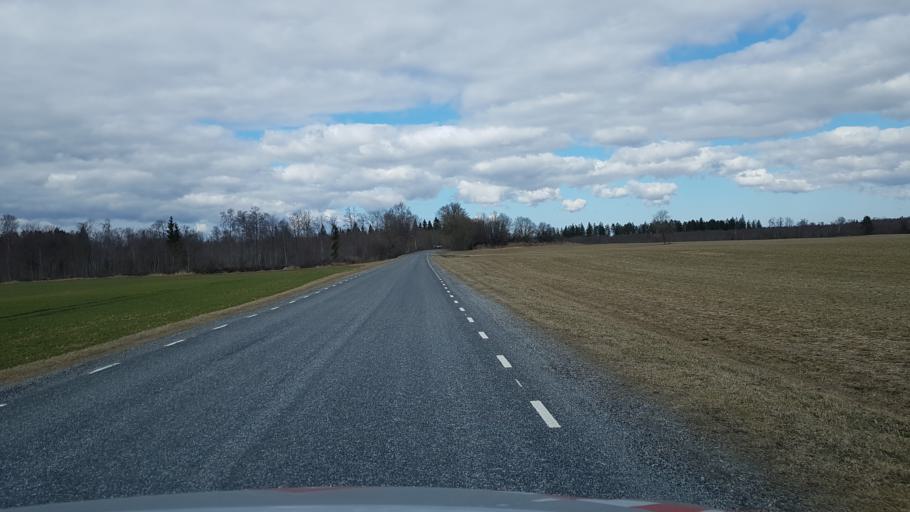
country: EE
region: Laeaene-Virumaa
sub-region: Tamsalu vald
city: Tamsalu
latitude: 59.1813
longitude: 26.1276
